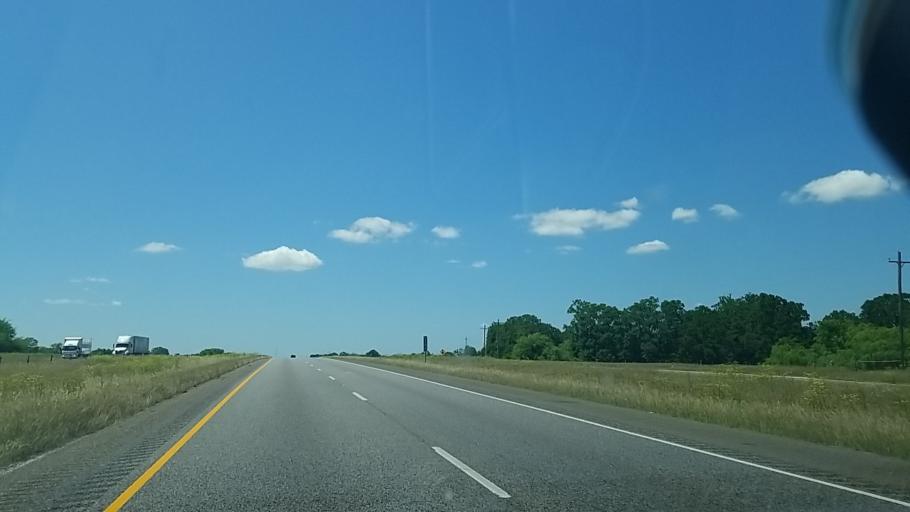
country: US
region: Texas
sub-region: Madison County
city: Madisonville
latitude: 30.9450
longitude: -95.8518
